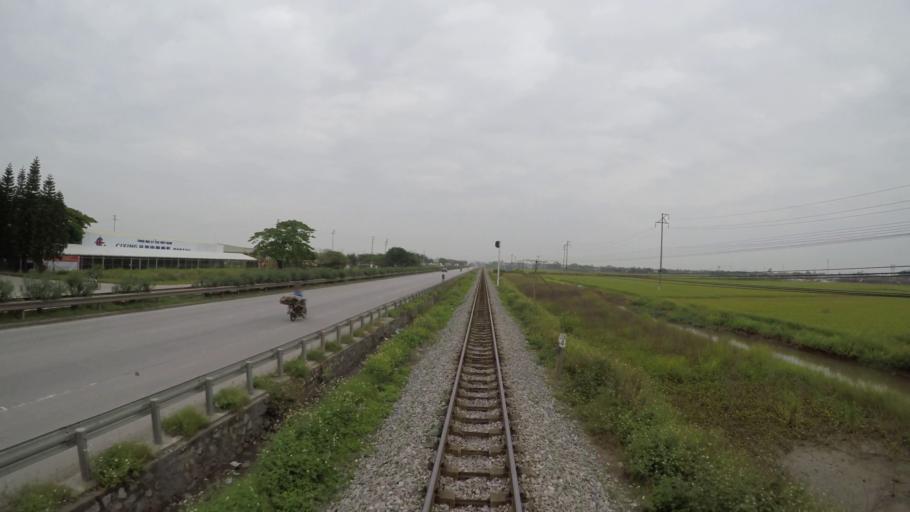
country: VN
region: Hai Duong
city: Phu Thai
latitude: 20.9636
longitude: 106.5170
